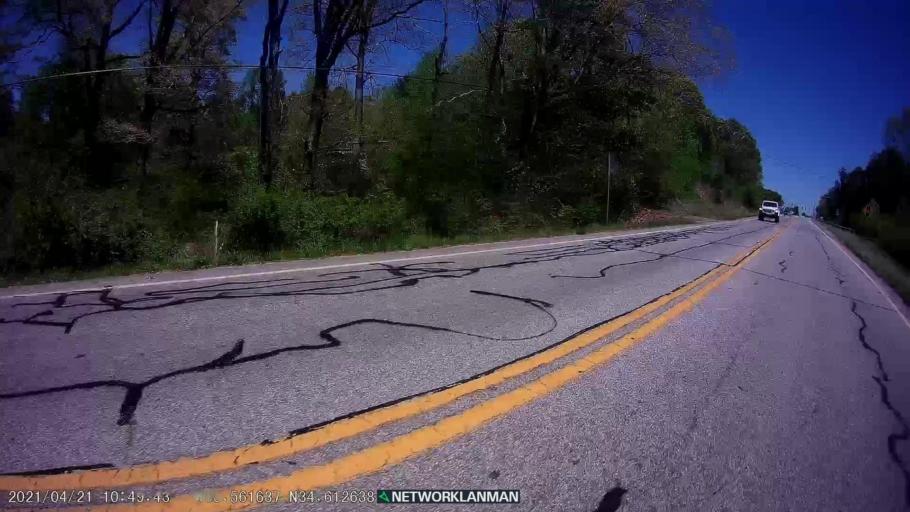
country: US
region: Georgia
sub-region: Habersham County
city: Clarkesville
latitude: 34.6129
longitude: -83.5611
